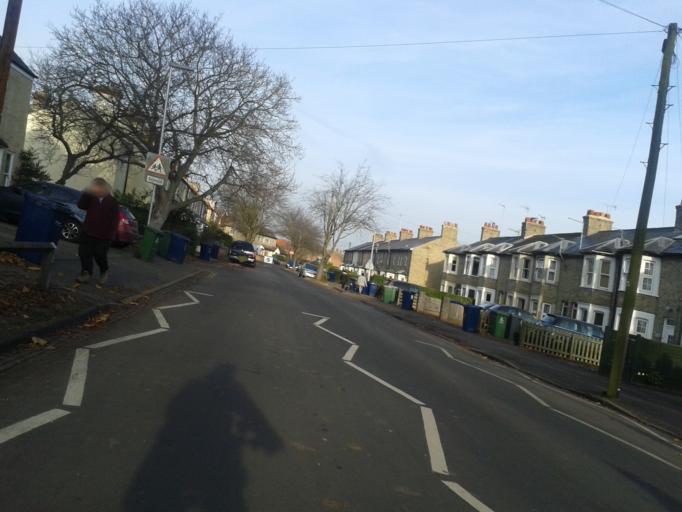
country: GB
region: England
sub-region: Cambridgeshire
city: Cambridge
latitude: 52.2004
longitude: 0.1524
